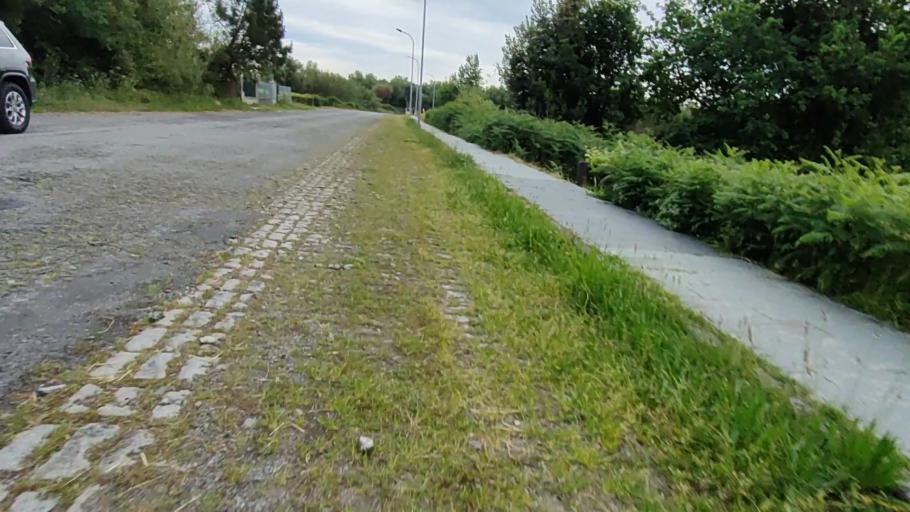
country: ES
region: Galicia
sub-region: Provincia da Coruna
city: Boiro
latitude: 42.6140
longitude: -8.8711
